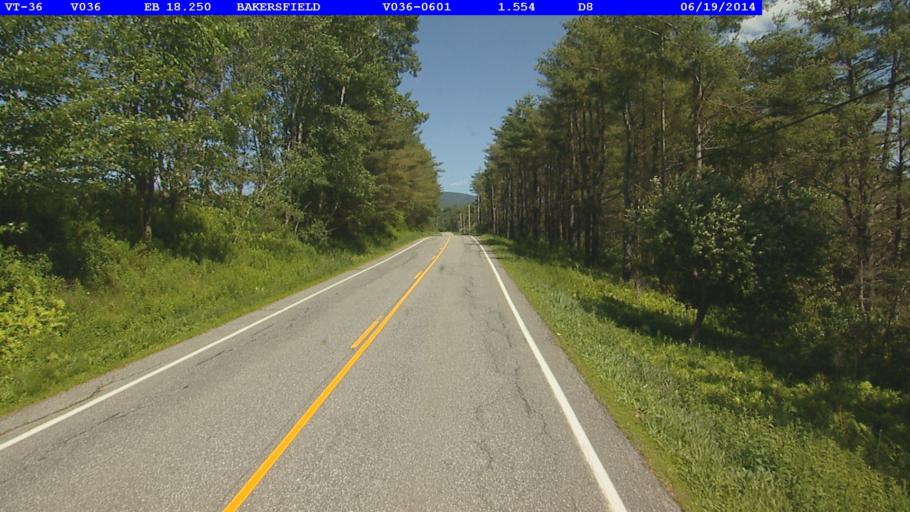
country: US
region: Vermont
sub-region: Franklin County
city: Enosburg Falls
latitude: 44.7812
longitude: -72.8199
